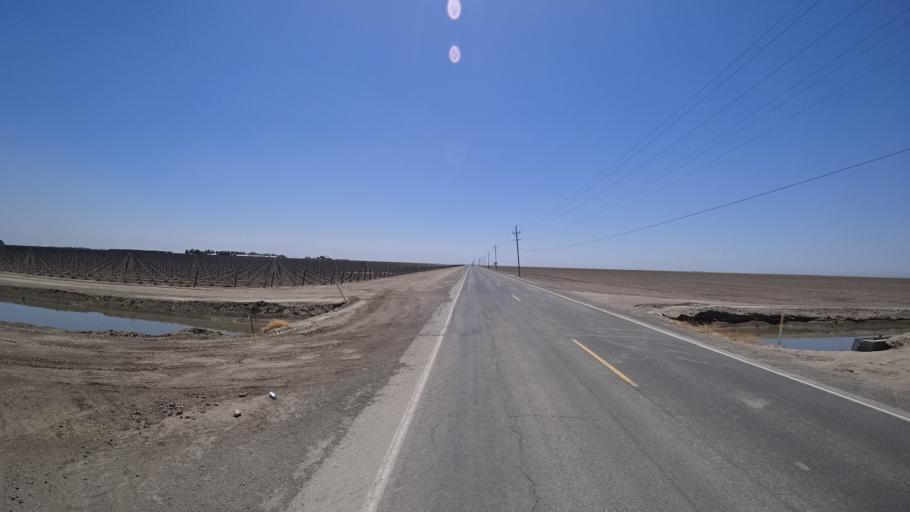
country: US
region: California
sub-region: Kings County
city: Corcoran
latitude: 36.1234
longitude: -119.6444
